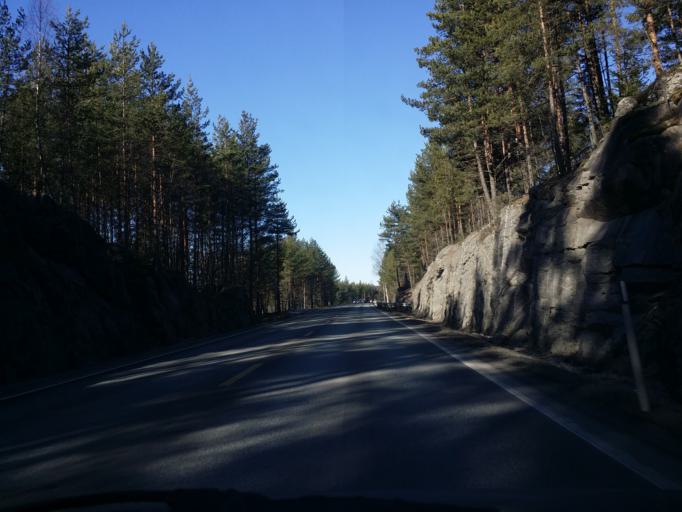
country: NO
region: Buskerud
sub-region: Ringerike
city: Honefoss
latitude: 60.2263
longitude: 10.2482
